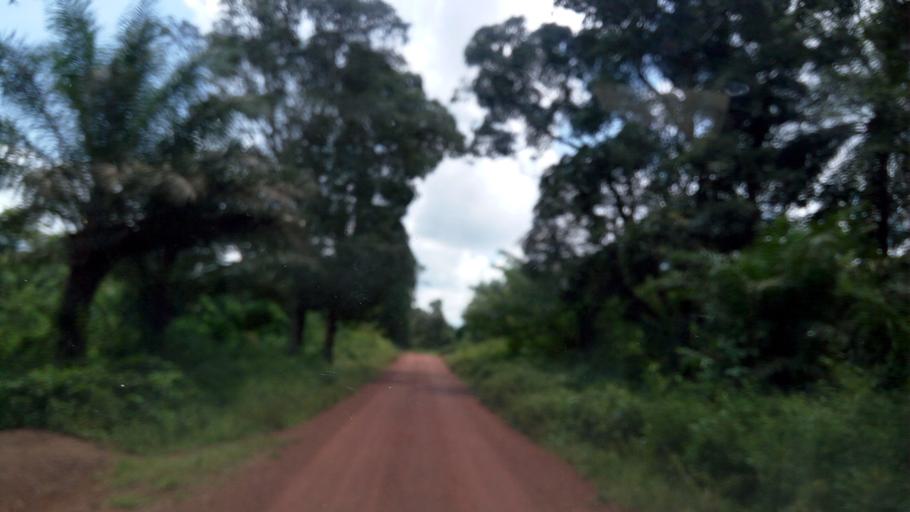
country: CD
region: Equateur
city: Libenge
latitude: 3.7764
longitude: 18.9280
